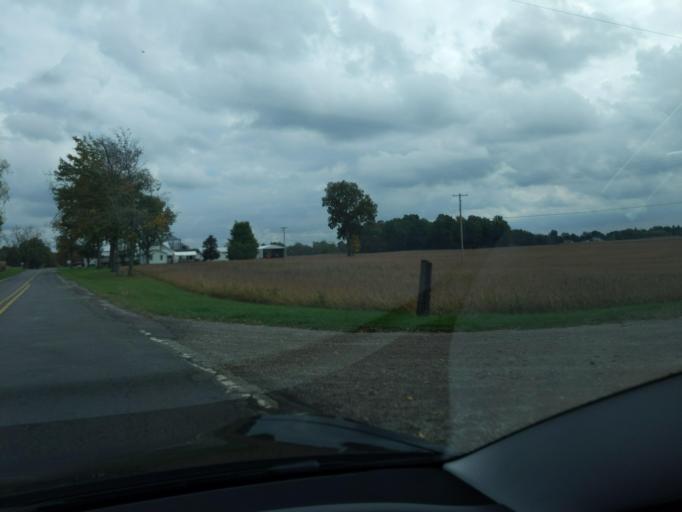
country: US
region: Michigan
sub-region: Ingham County
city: Leslie
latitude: 42.4127
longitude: -84.3632
